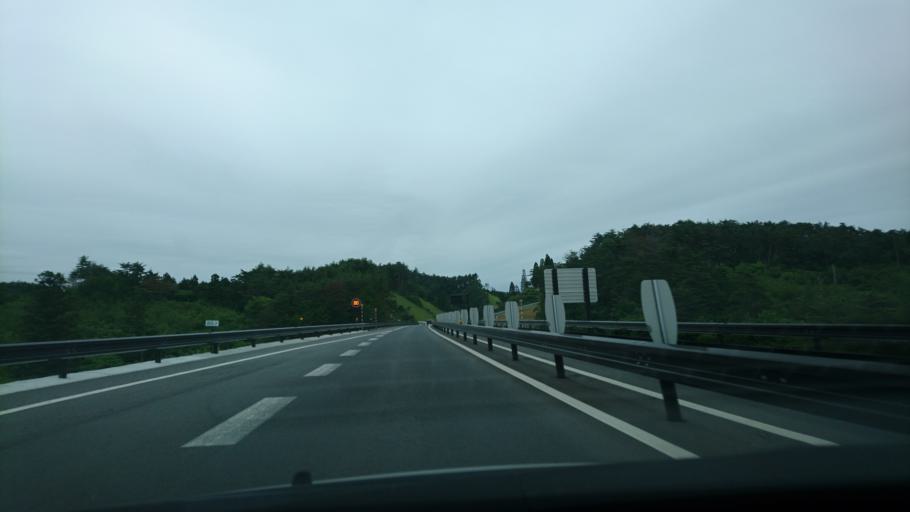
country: JP
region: Miyagi
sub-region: Oshika Gun
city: Onagawa Cho
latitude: 38.6956
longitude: 141.4662
